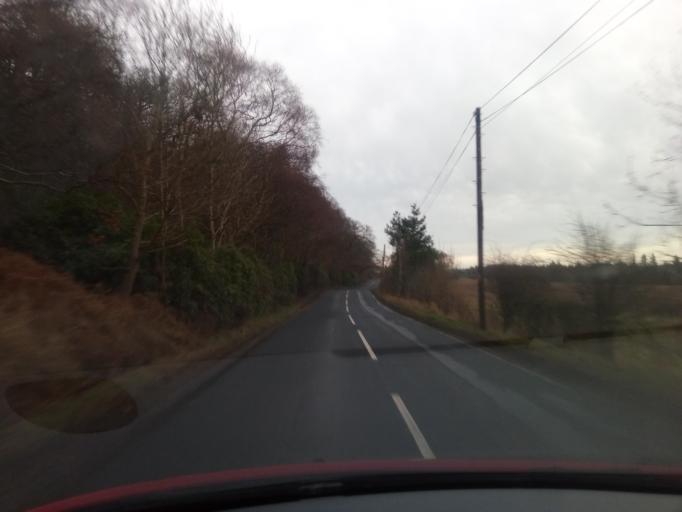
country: GB
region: England
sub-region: Northumberland
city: Whittingham
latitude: 55.4750
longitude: -1.8611
